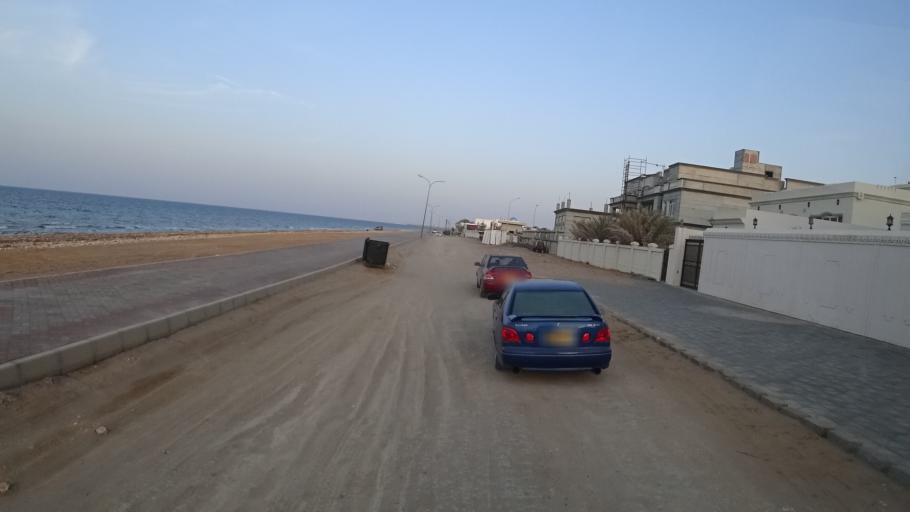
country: OM
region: Ash Sharqiyah
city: Sur
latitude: 22.5929
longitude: 59.4995
